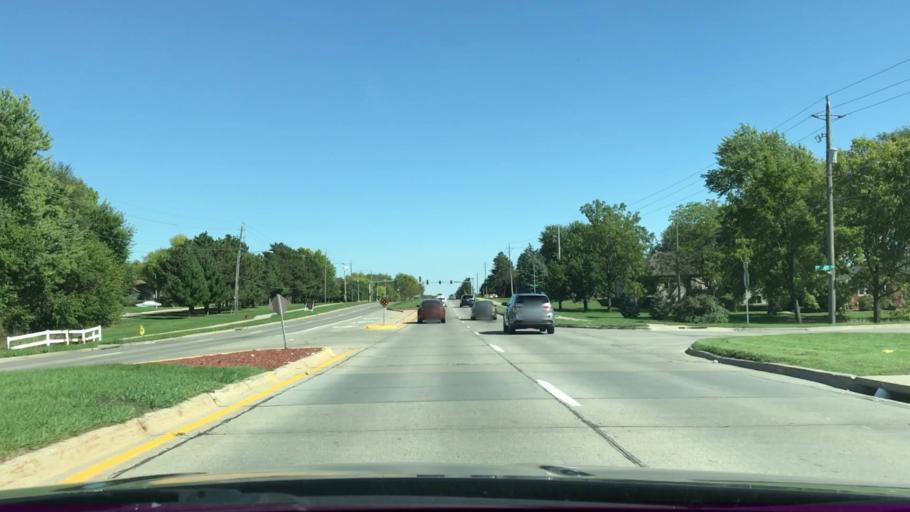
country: US
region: Iowa
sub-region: Polk County
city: Altoona
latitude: 41.6441
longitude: -93.4938
